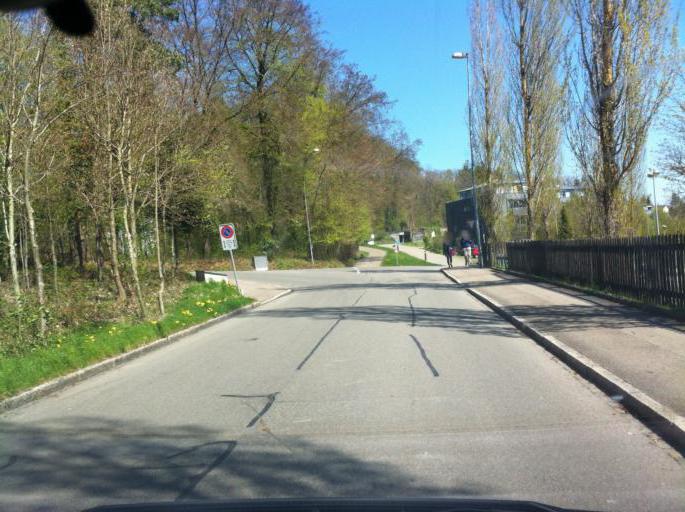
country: CH
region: Schaffhausen
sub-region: Bezirk Schaffhausen
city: Schaffhausen
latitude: 47.7125
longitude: 8.6391
